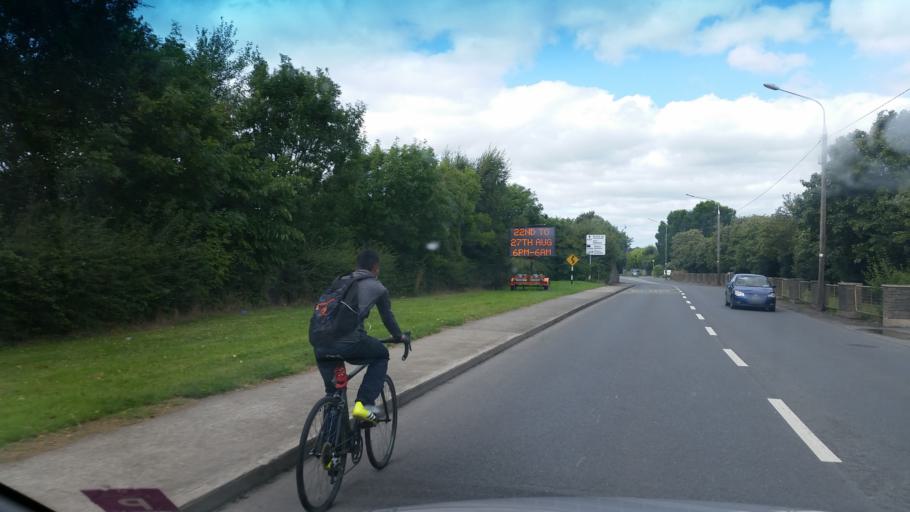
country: IE
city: Darndale
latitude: 53.4218
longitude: -6.1764
